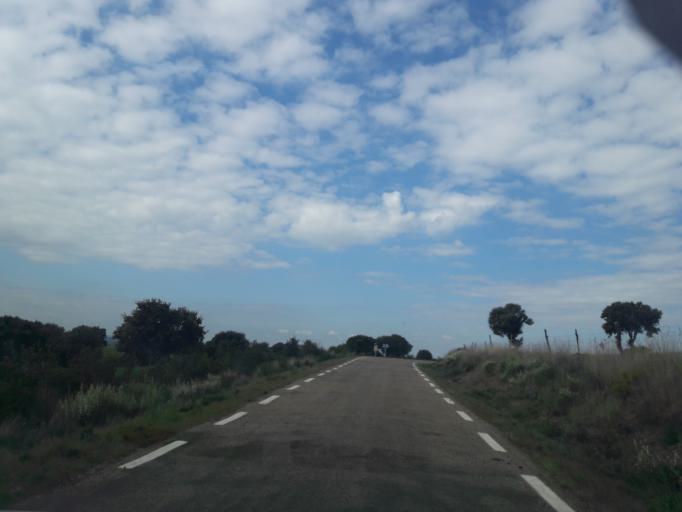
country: ES
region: Castille and Leon
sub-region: Provincia de Salamanca
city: Zamarra
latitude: 40.5439
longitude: -6.4120
